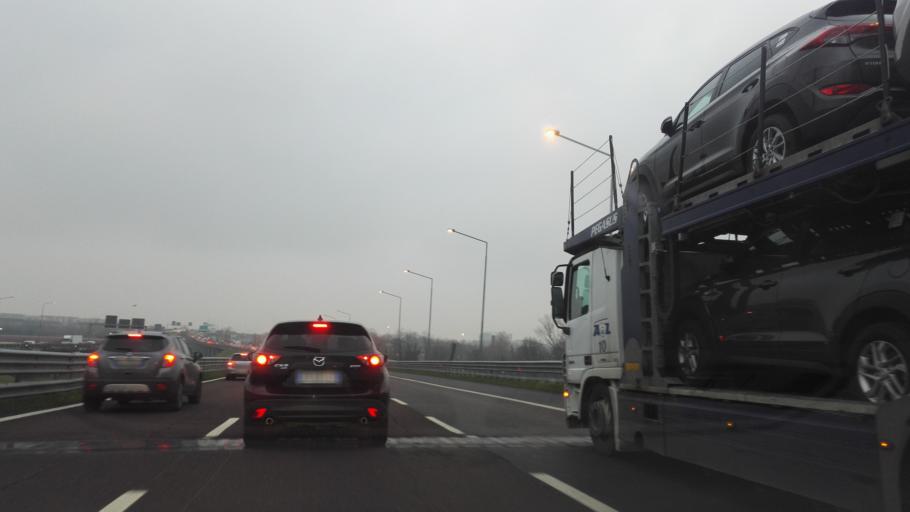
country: IT
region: Lombardy
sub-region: Citta metropolitana di Milano
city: Linate
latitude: 45.4637
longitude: 9.2519
